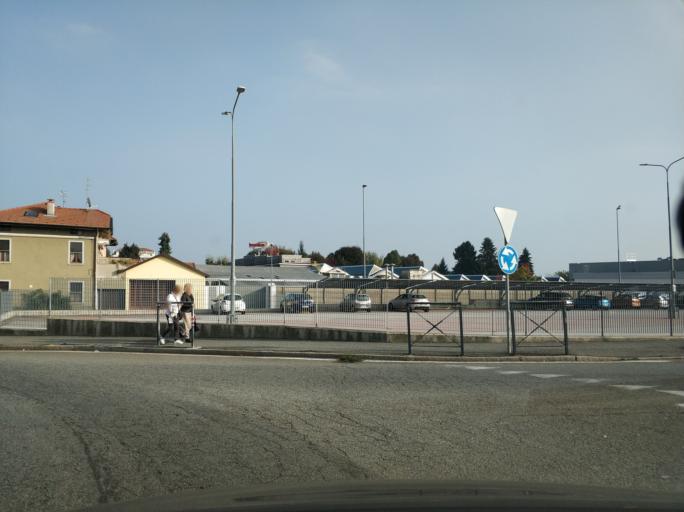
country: IT
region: Piedmont
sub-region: Provincia di Biella
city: Ronco Biellese
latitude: 45.5656
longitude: 8.0915
